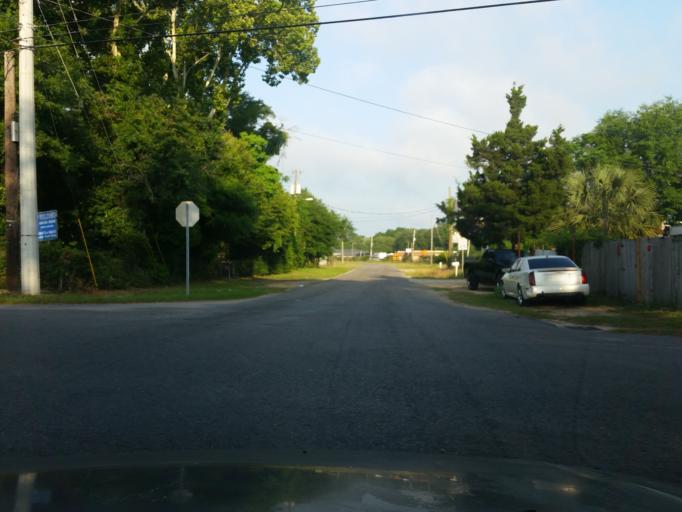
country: US
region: Florida
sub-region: Escambia County
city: West Pensacola
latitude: 30.4371
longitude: -87.2614
